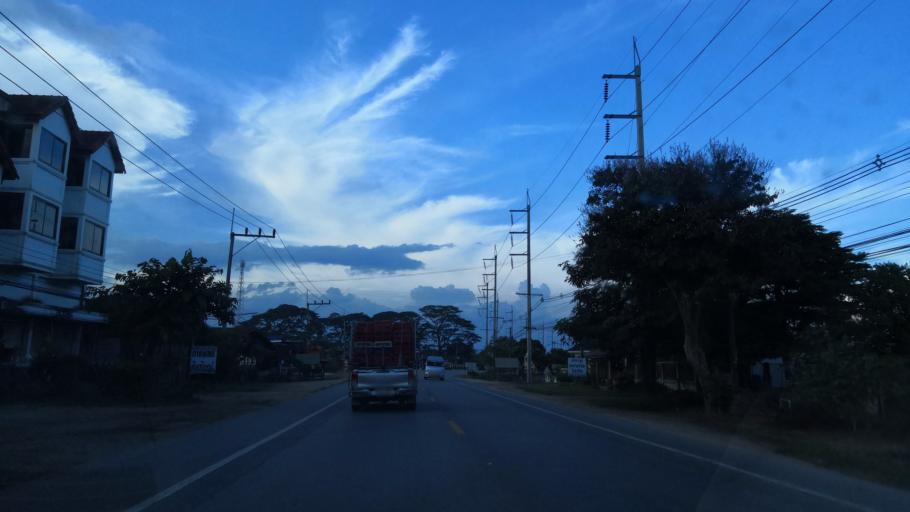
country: TH
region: Chiang Rai
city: Mae Suai
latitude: 19.5669
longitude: 99.4928
